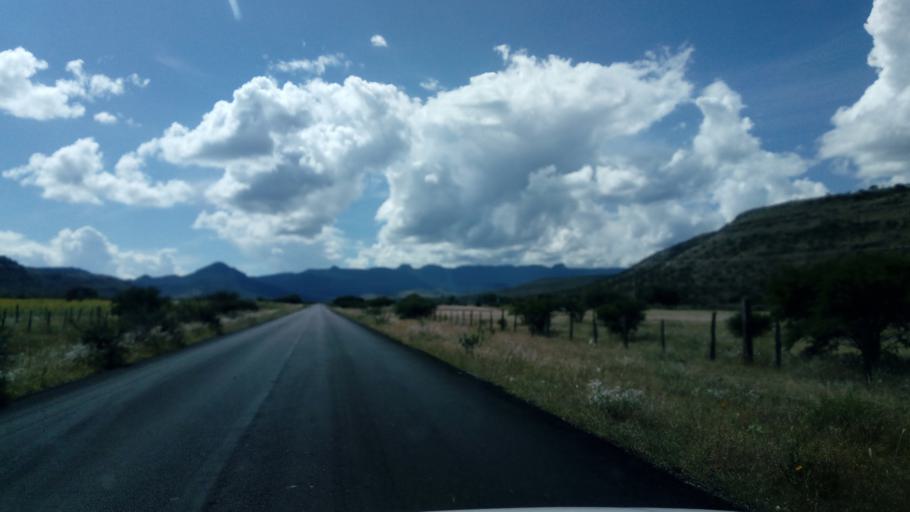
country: MX
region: Durango
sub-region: Durango
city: Jose Refugio Salcido
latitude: 23.8167
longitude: -104.4833
